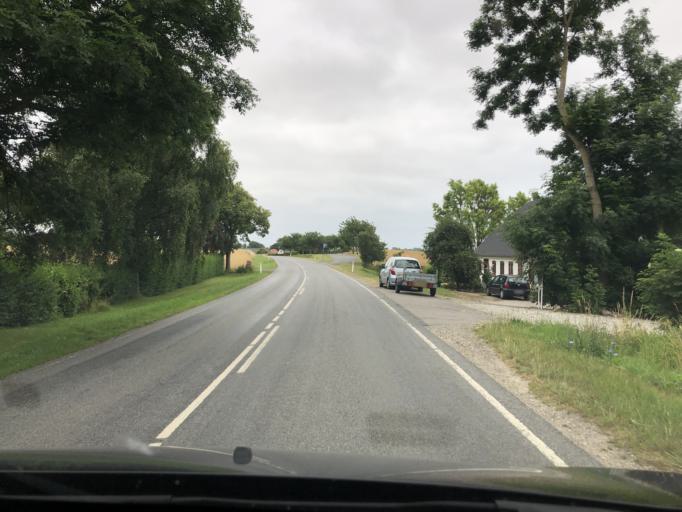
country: DK
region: South Denmark
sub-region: AEro Kommune
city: AEroskobing
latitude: 54.9318
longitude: 10.2650
